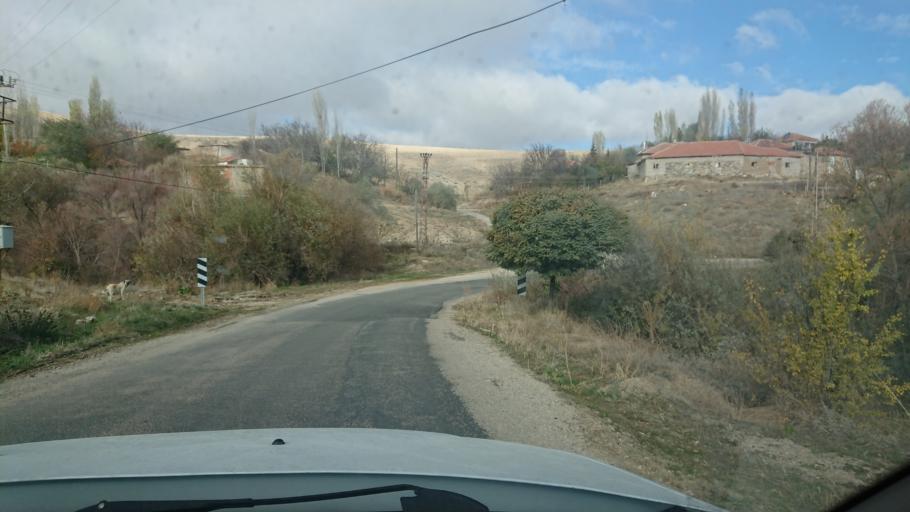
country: TR
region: Aksaray
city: Ortakoy
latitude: 38.8049
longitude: 33.9823
